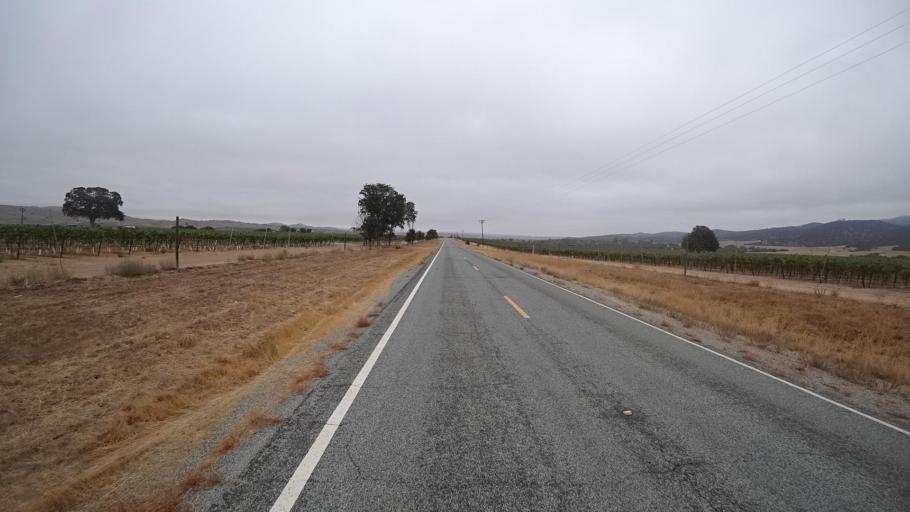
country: US
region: California
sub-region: San Luis Obispo County
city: Lake Nacimiento
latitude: 35.8829
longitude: -120.9094
